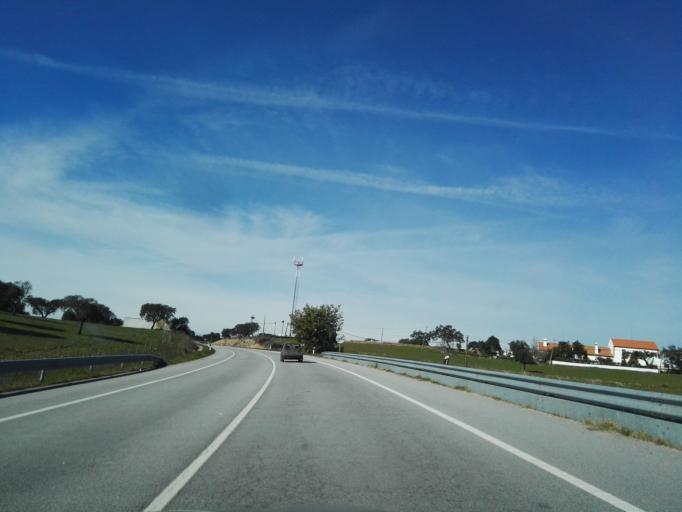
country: PT
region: Portalegre
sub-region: Portalegre
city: Urra
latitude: 39.2054
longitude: -7.3678
